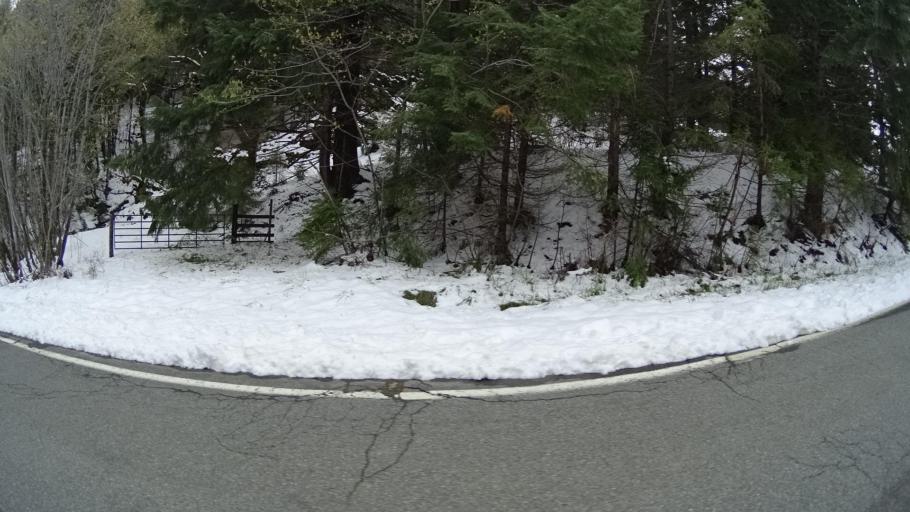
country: US
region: California
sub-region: Humboldt County
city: Willow Creek
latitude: 40.8735
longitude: -123.7537
